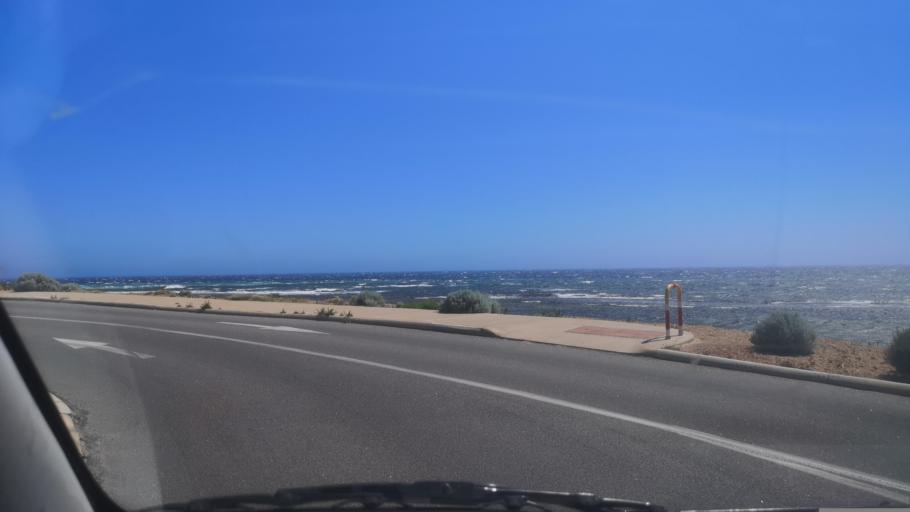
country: AU
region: Western Australia
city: Port Denison
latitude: -29.2772
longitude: 114.9148
